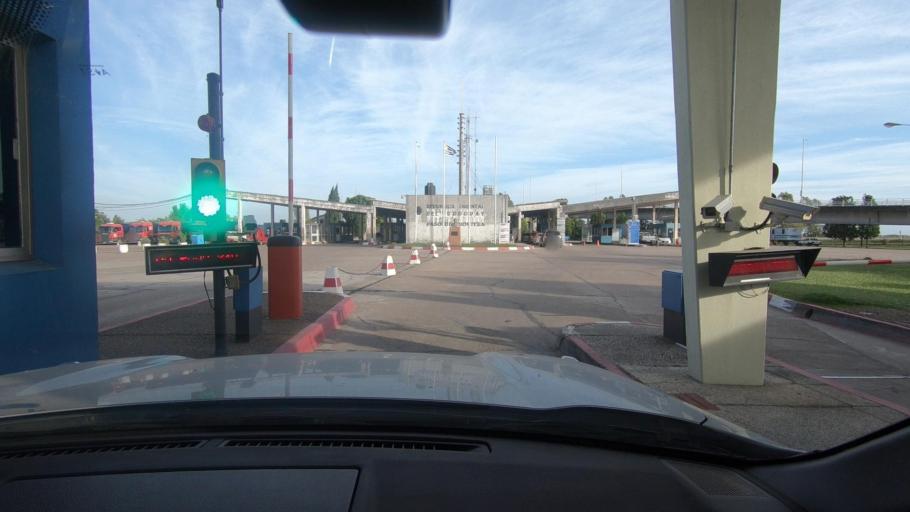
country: AR
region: Entre Rios
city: Colon
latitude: -32.2583
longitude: -58.1358
